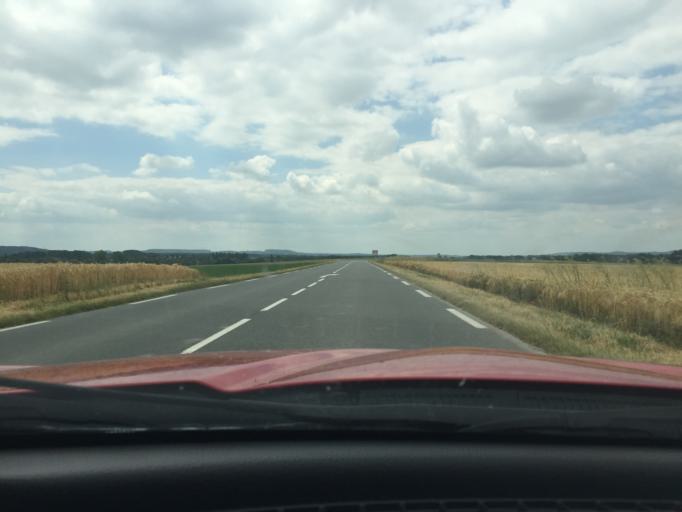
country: FR
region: Champagne-Ardenne
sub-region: Departement de la Marne
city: Cormicy
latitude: 49.4150
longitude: 3.9016
